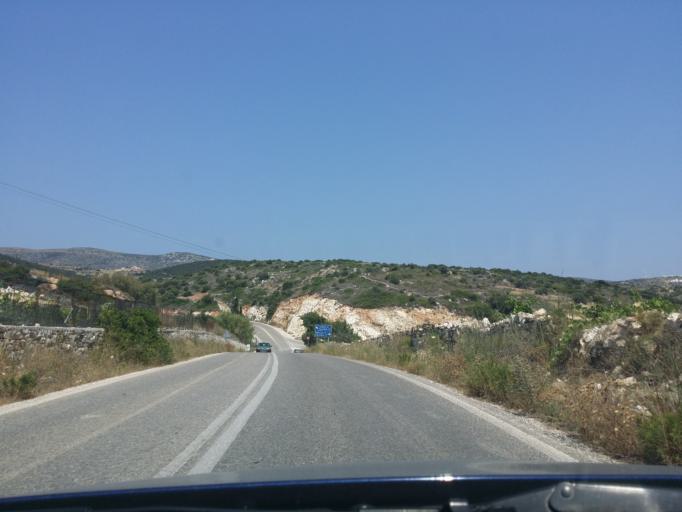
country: GR
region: South Aegean
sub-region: Nomos Kykladon
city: Naousa
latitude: 37.0606
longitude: 25.2350
